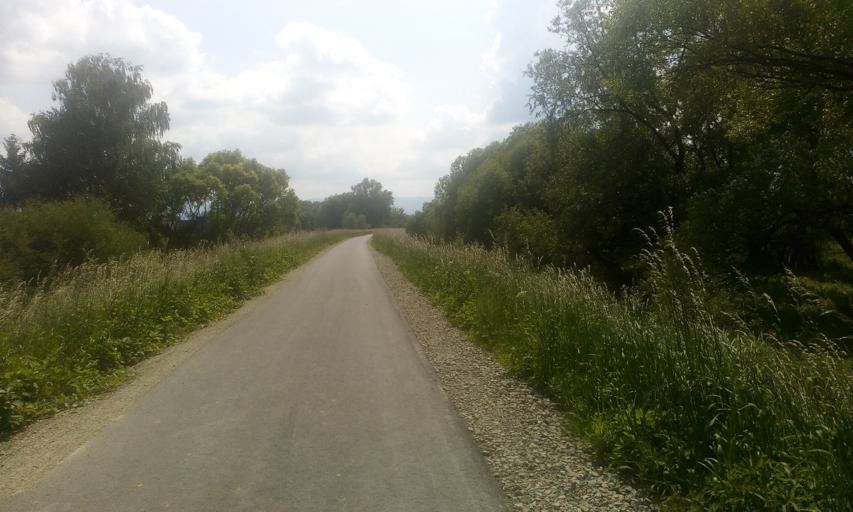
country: PL
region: Lesser Poland Voivodeship
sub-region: Powiat nowosadecki
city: Nowy Sacz
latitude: 49.6143
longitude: 20.6824
